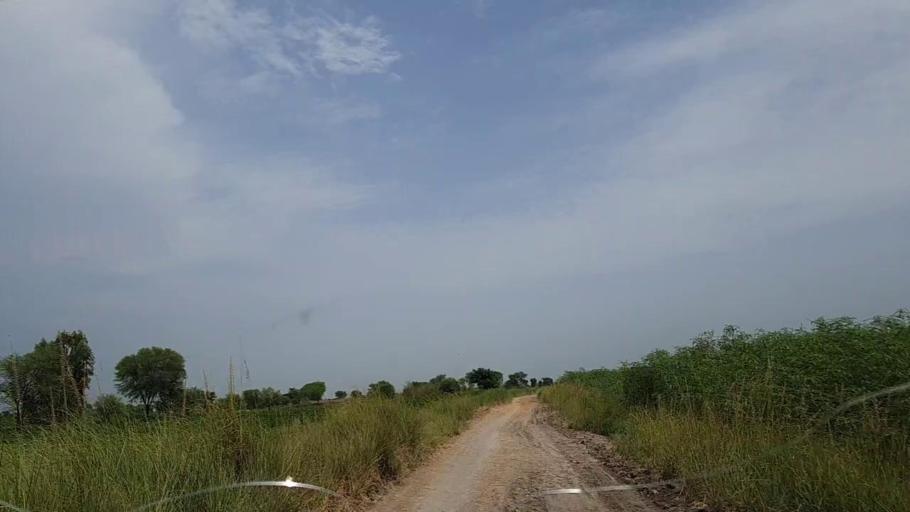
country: PK
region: Sindh
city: Naushahro Firoz
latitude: 26.8892
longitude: 68.0760
